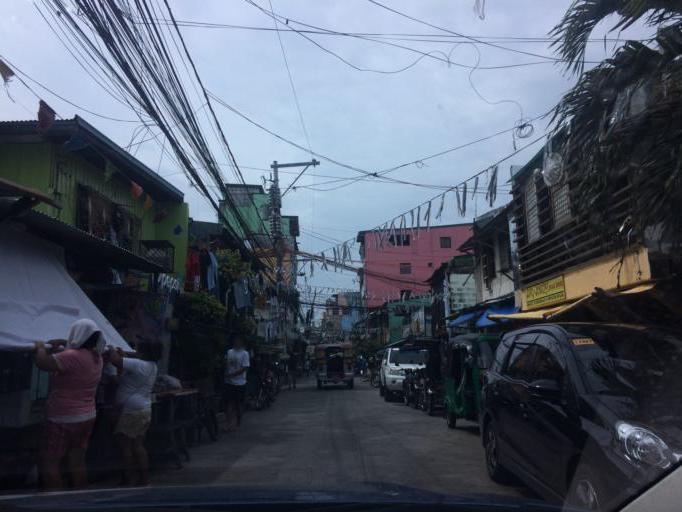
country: PH
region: Metro Manila
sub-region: Makati City
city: Makati City
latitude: 14.5458
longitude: 121.0026
